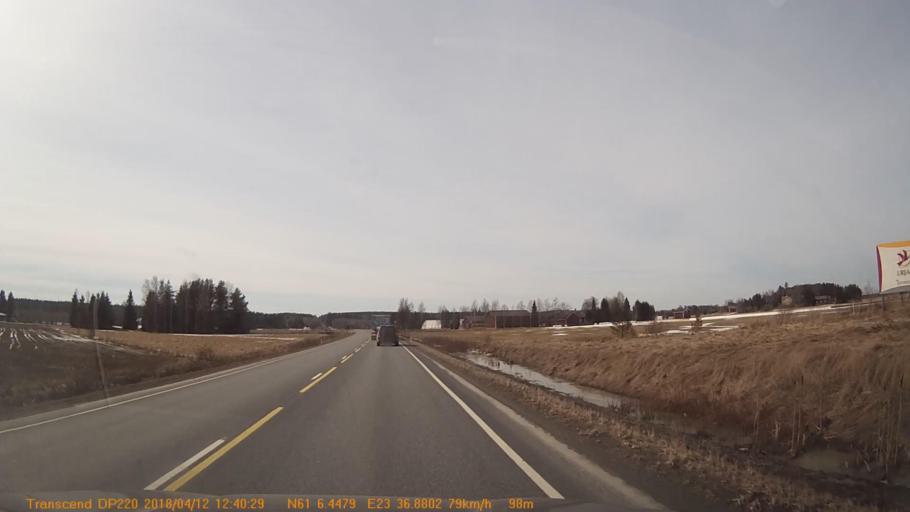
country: FI
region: Pirkanmaa
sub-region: Etelae-Pirkanmaa
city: Urjala
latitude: 61.1073
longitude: 23.6152
